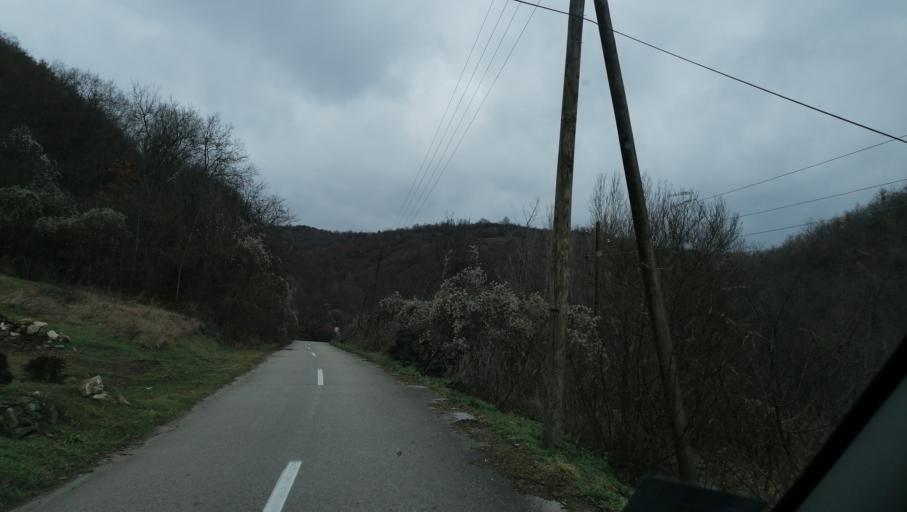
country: RS
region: Central Serbia
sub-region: Pirotski Okrug
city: Dimitrovgrad
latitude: 42.9262
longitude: 22.7562
